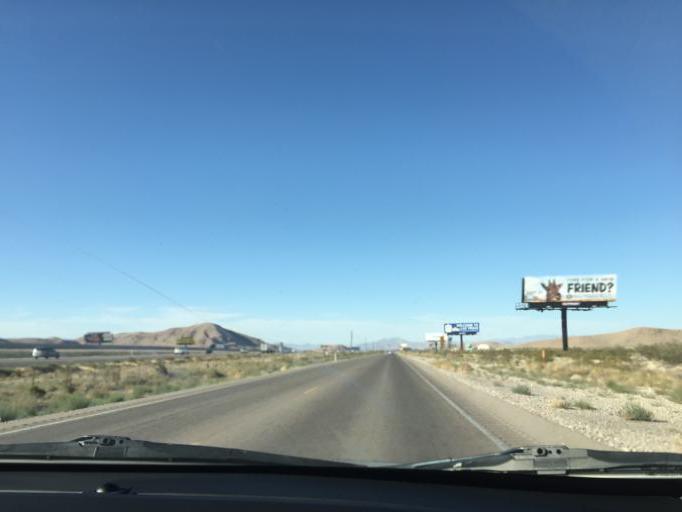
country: US
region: Nevada
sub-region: Clark County
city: Enterprise
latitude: 35.9165
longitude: -115.2022
